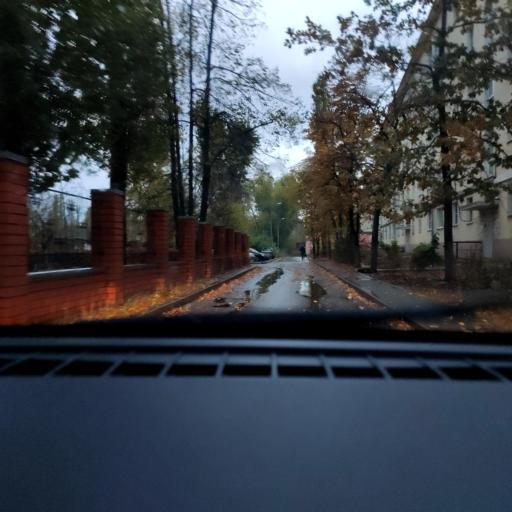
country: RU
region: Voronezj
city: Voronezh
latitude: 51.6894
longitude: 39.2644
